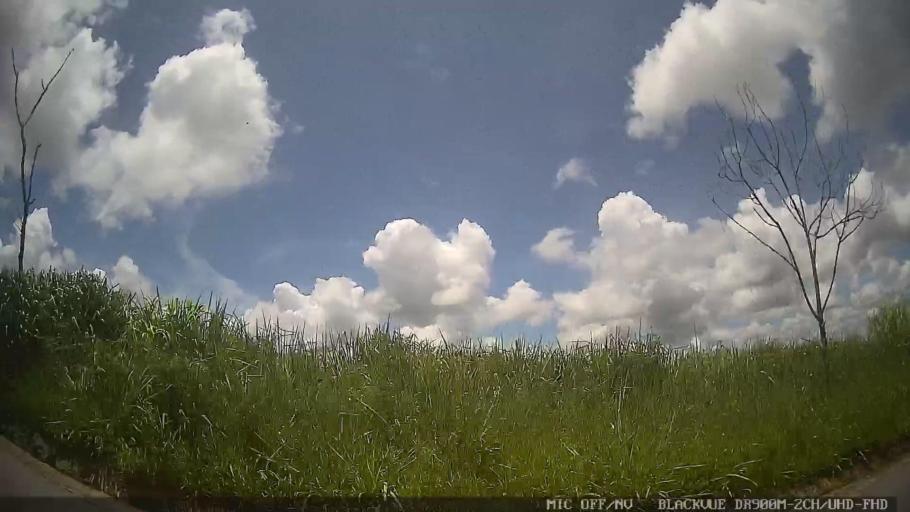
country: BR
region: Sao Paulo
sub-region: Amparo
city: Amparo
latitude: -22.7841
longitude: -46.7150
